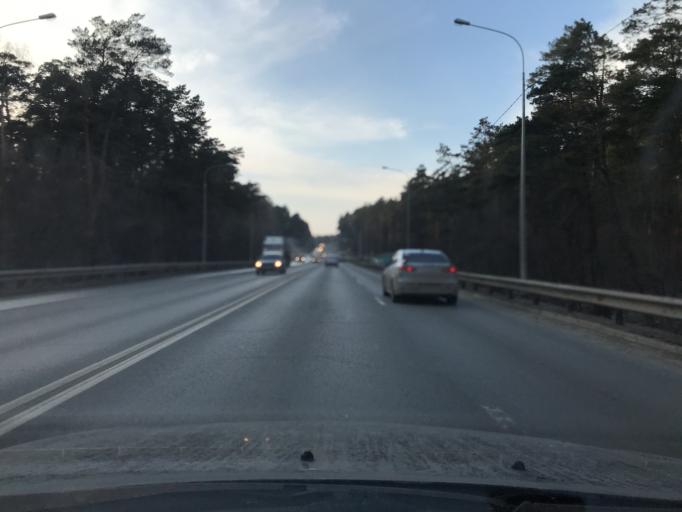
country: RU
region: Kaluga
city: Kaluga
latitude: 54.5158
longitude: 36.2053
